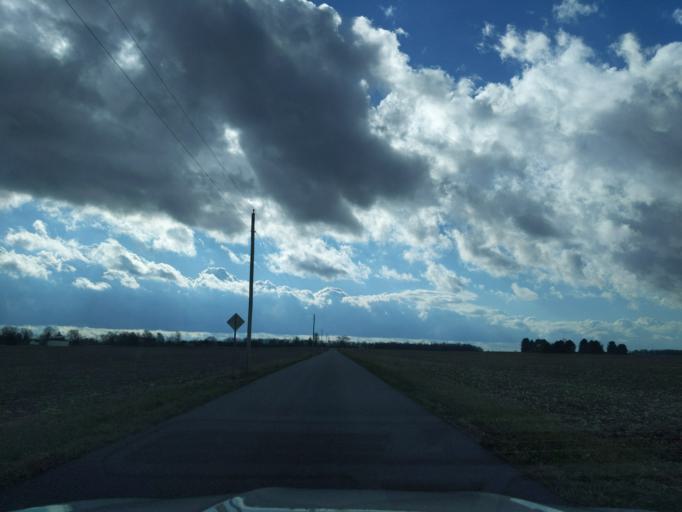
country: US
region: Indiana
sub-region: Decatur County
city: Greensburg
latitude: 39.3793
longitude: -85.5032
